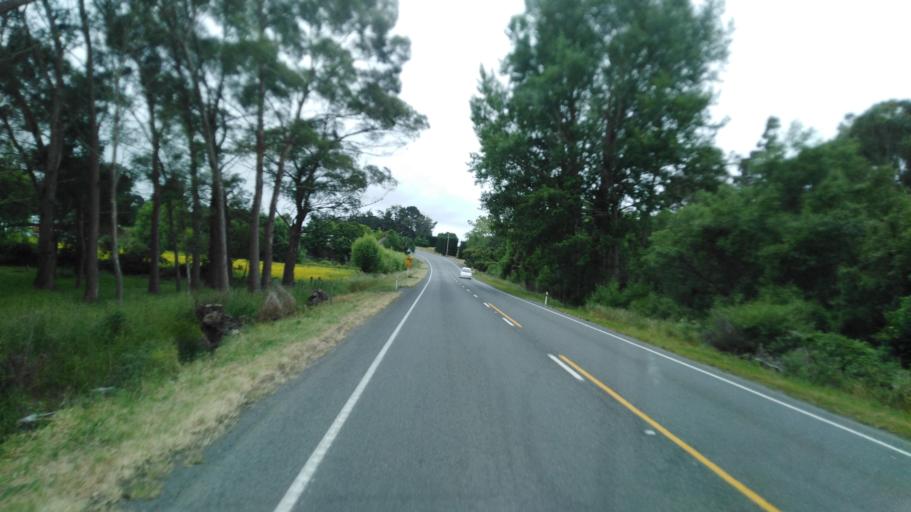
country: NZ
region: Canterbury
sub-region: Hurunui District
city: Amberley
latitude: -43.1865
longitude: 172.7484
